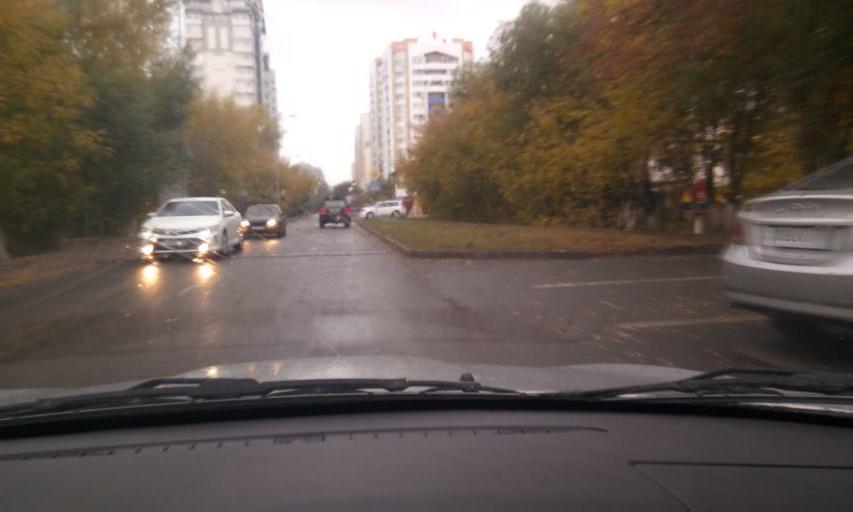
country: KZ
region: Astana Qalasy
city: Astana
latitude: 51.1597
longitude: 71.4330
